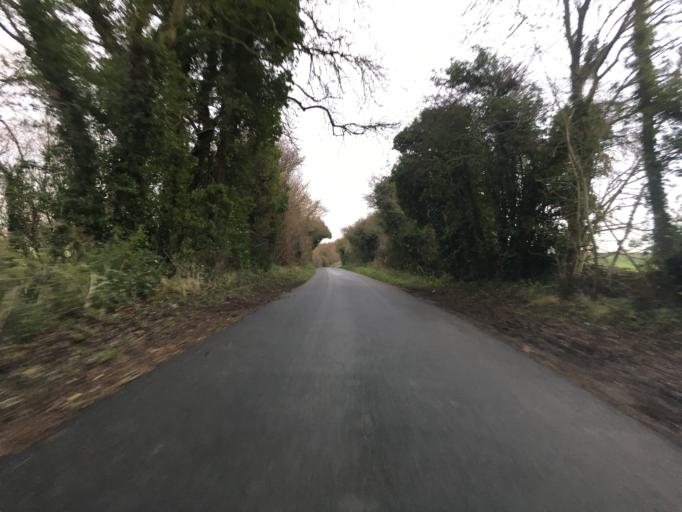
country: GB
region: England
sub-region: South Gloucestershire
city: Marshfield
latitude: 51.5006
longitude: -2.3165
